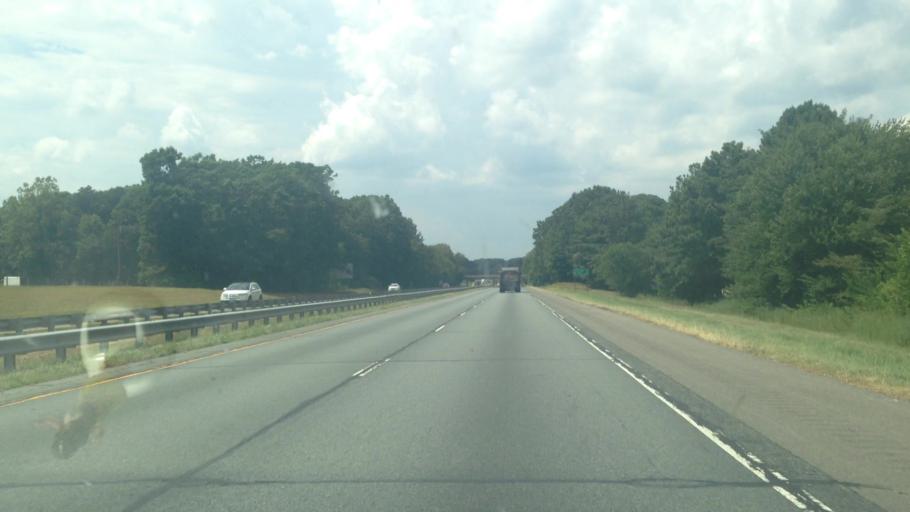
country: US
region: North Carolina
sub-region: Stokes County
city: King
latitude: 36.2683
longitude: -80.3727
